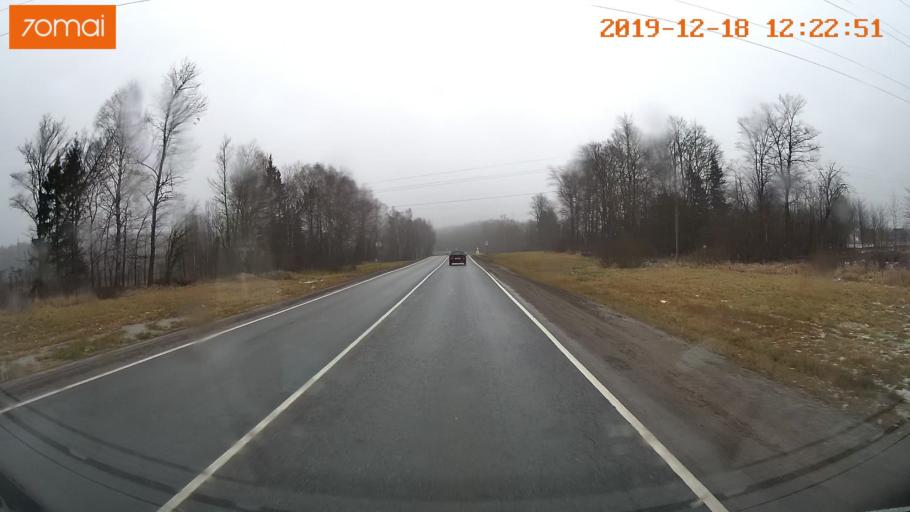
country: RU
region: Moskovskaya
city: Novopetrovskoye
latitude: 56.0089
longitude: 36.4852
